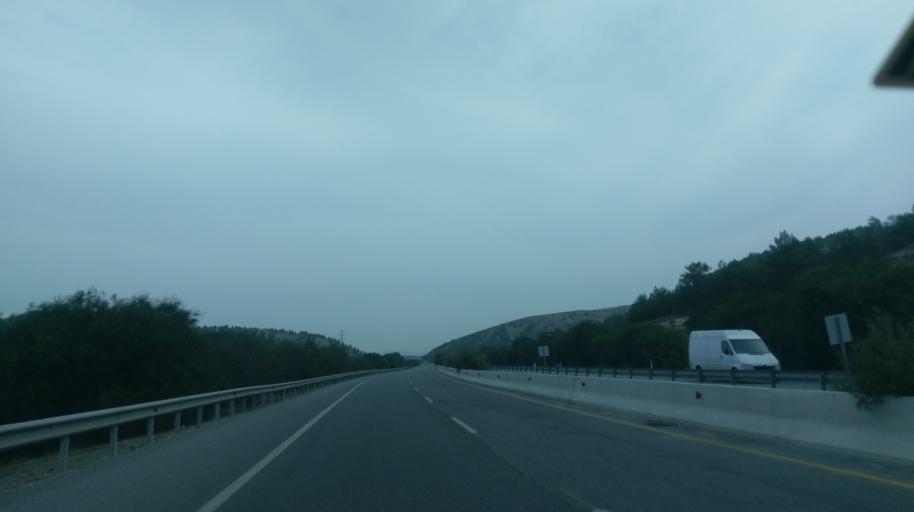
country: CY
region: Lefkosia
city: Akaki
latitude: 35.2054
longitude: 33.1180
